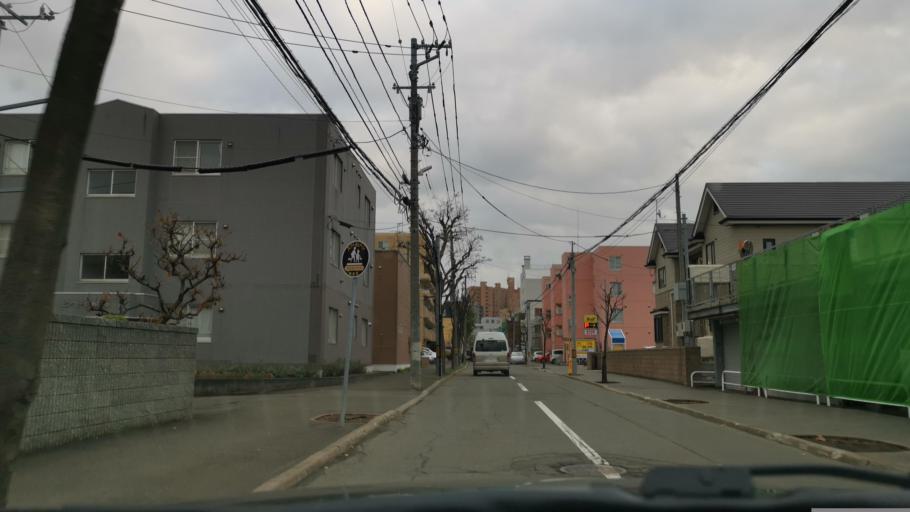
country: JP
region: Hokkaido
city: Sapporo
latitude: 43.0499
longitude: 141.3935
